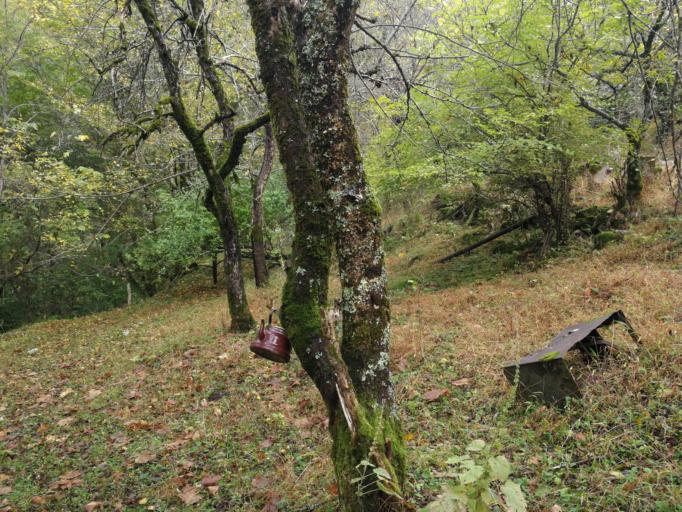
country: GE
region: Abkhazia
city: Gagra
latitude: 43.3290
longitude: 40.2651
